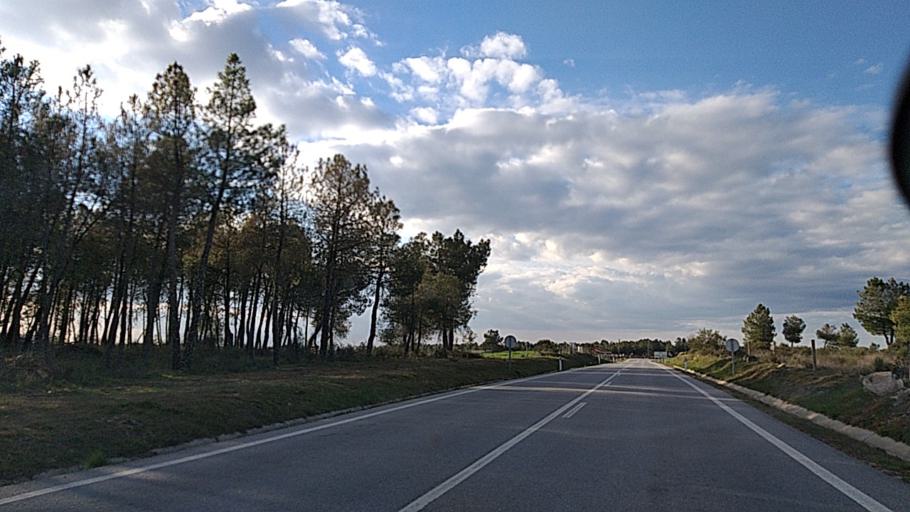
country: ES
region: Castille and Leon
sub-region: Provincia de Salamanca
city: Aldea del Obispo
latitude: 40.6706
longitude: -6.8601
